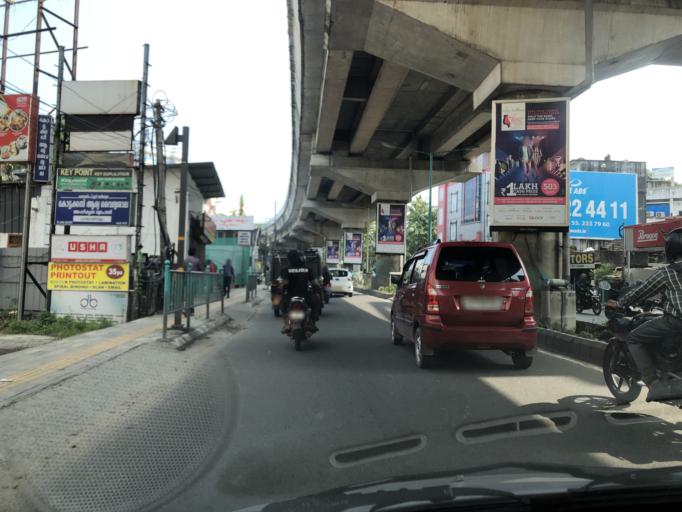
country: IN
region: Kerala
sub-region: Ernakulam
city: Elur
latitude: 10.0021
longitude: 76.3036
